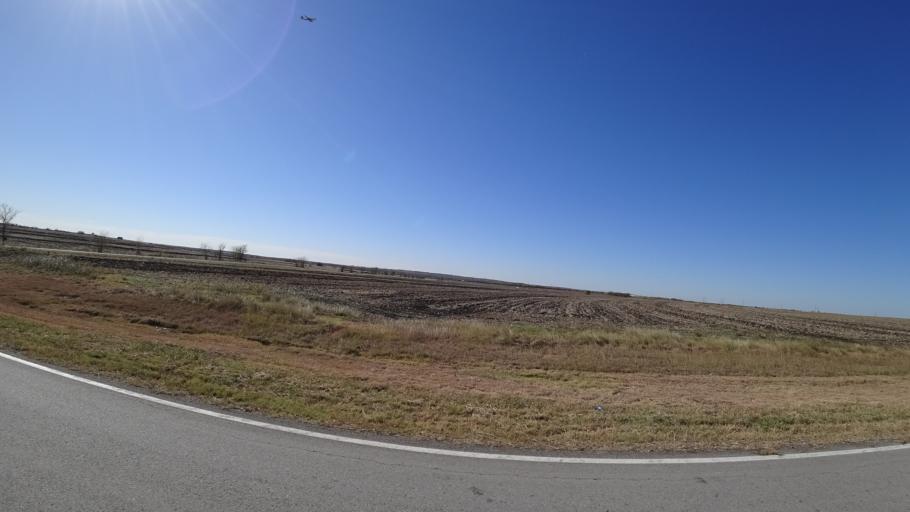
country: US
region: Texas
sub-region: Travis County
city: Garfield
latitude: 30.0997
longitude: -97.6374
